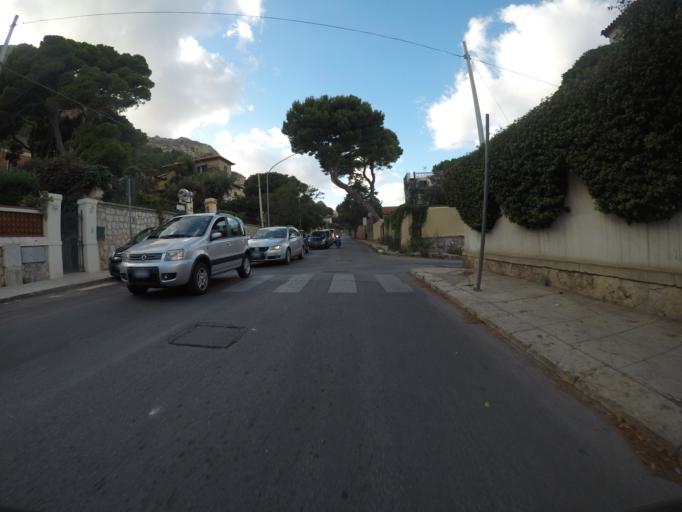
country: IT
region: Sicily
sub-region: Palermo
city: Isola delle Femmine
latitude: 38.1985
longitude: 13.2710
